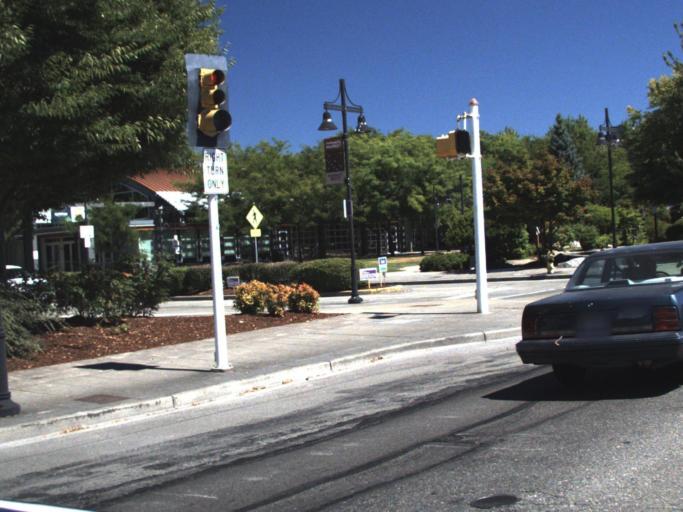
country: US
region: Washington
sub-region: King County
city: Renton
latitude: 47.4797
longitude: -122.2094
